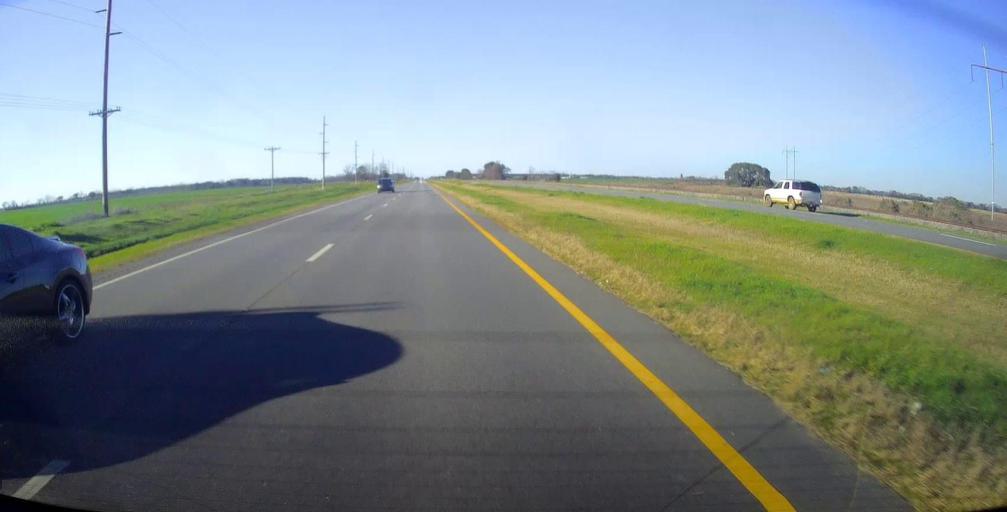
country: US
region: Georgia
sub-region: Lee County
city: Leesburg
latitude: 31.7693
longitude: -84.1898
